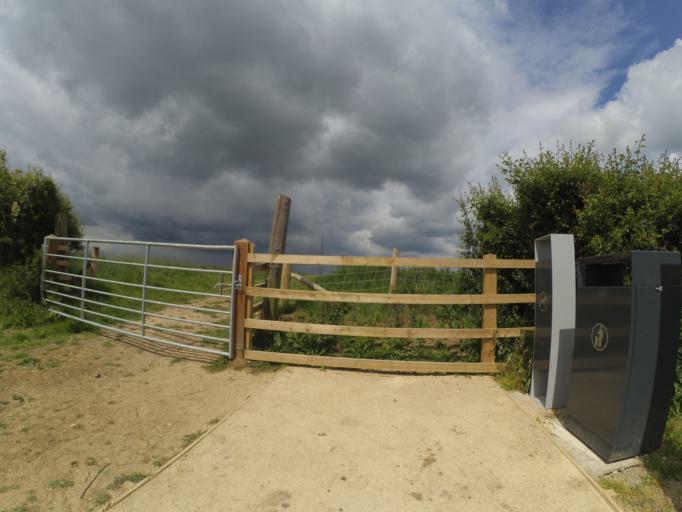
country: GB
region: England
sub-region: Warwickshire
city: Rugby
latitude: 52.3610
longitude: -1.1953
